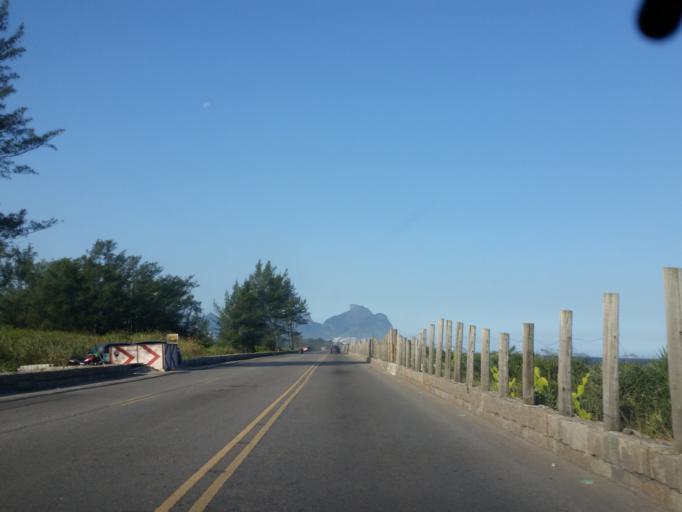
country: BR
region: Rio de Janeiro
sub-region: Nilopolis
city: Nilopolis
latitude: -23.0169
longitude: -43.4200
